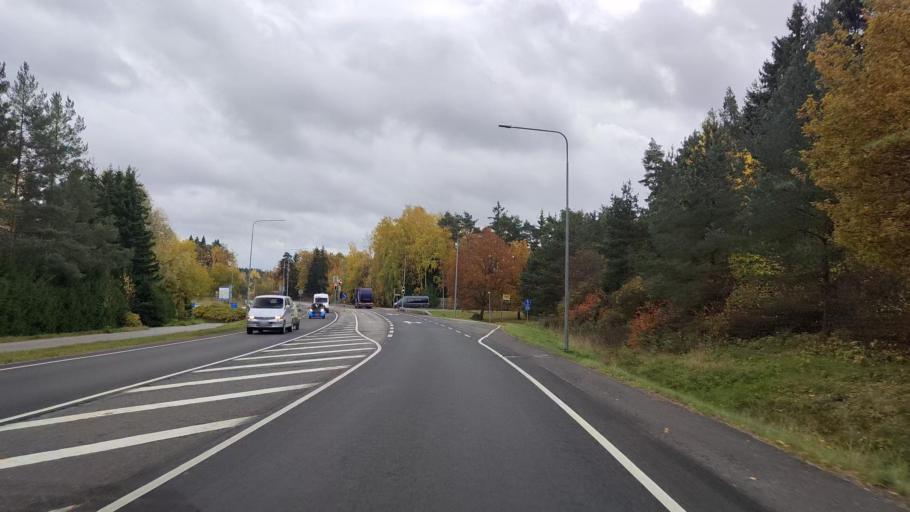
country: FI
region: Varsinais-Suomi
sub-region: Turku
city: Kaarina
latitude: 60.4472
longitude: 22.3742
